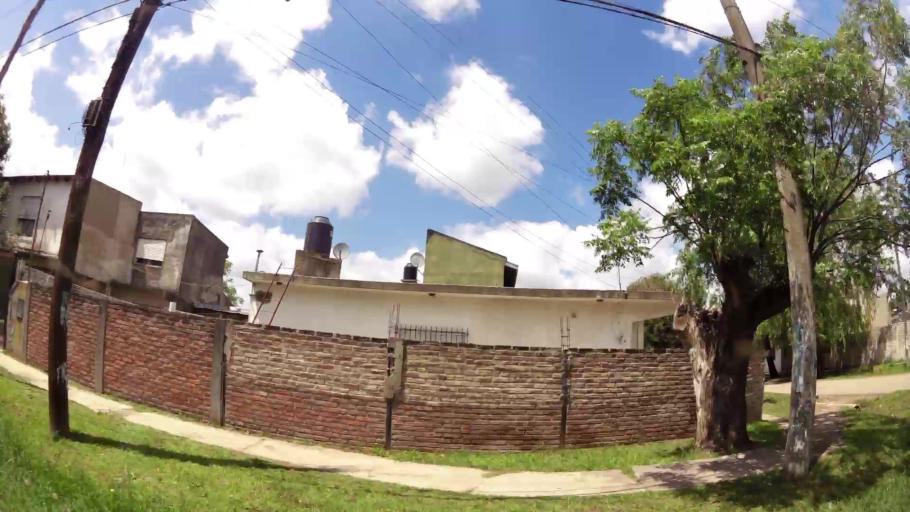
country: AR
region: Buenos Aires
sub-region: Partido de Quilmes
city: Quilmes
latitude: -34.8201
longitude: -58.2457
